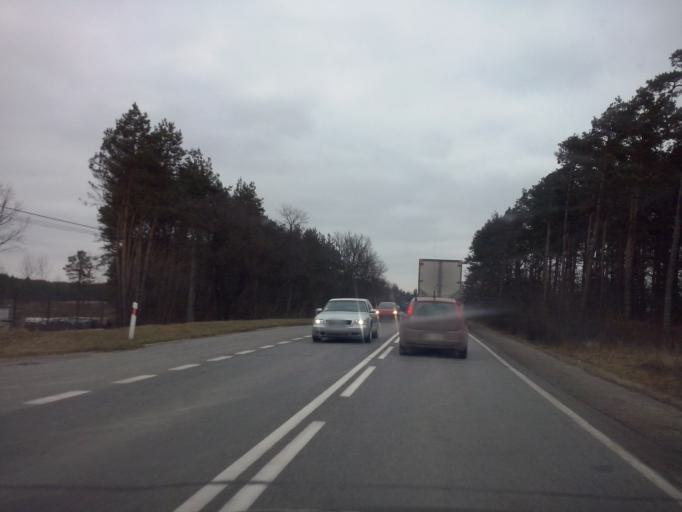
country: PL
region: Subcarpathian Voivodeship
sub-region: Powiat nizanski
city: Rudnik nad Sanem
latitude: 50.4567
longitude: 22.2427
